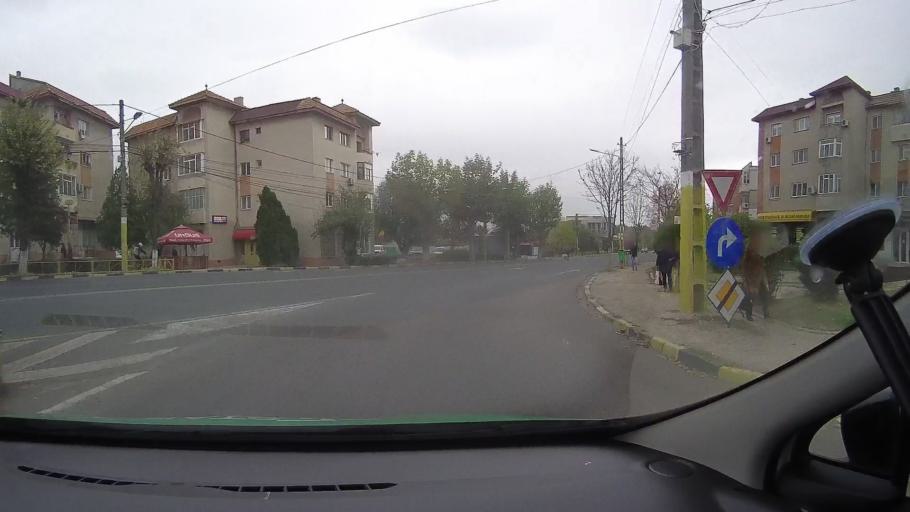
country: RO
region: Constanta
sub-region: Oras Murfatlar
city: Murfatlar
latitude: 44.1742
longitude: 28.4109
